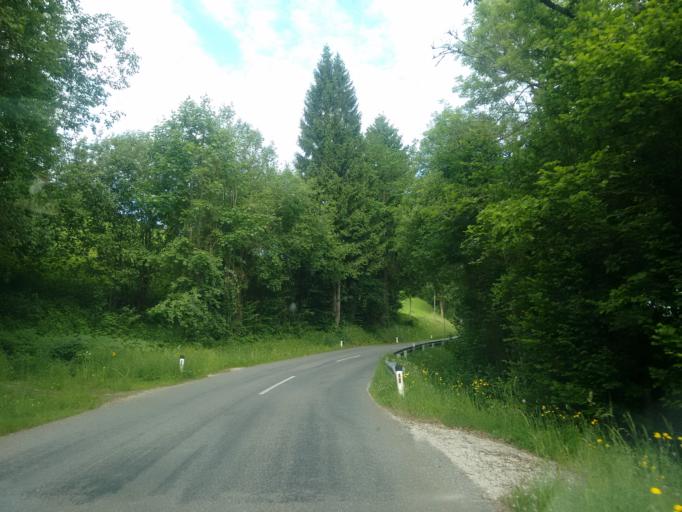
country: AT
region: Upper Austria
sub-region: Politischer Bezirk Kirchdorf an der Krems
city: Rossleithen
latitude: 47.6953
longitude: 14.3077
